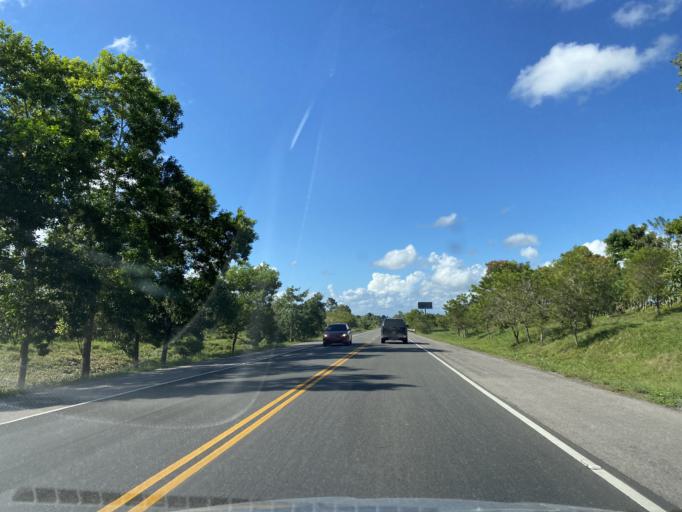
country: DO
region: Monte Plata
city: Sabana Grande de Boya
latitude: 18.9801
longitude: -69.8000
